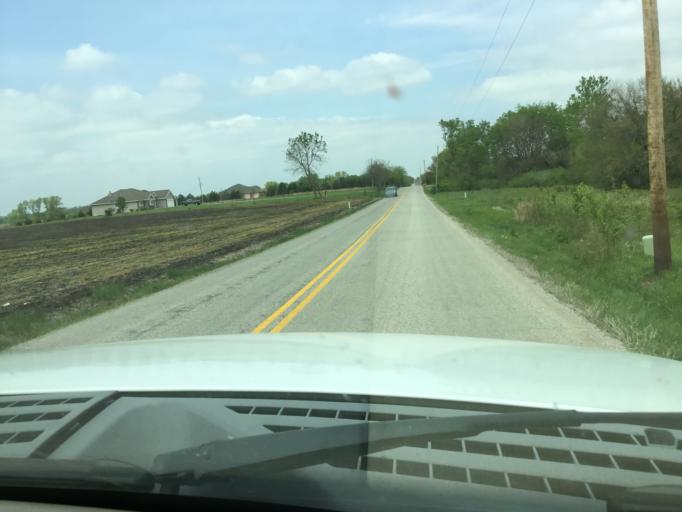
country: US
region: Kansas
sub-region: Shawnee County
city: Topeka
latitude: 38.9631
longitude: -95.6142
